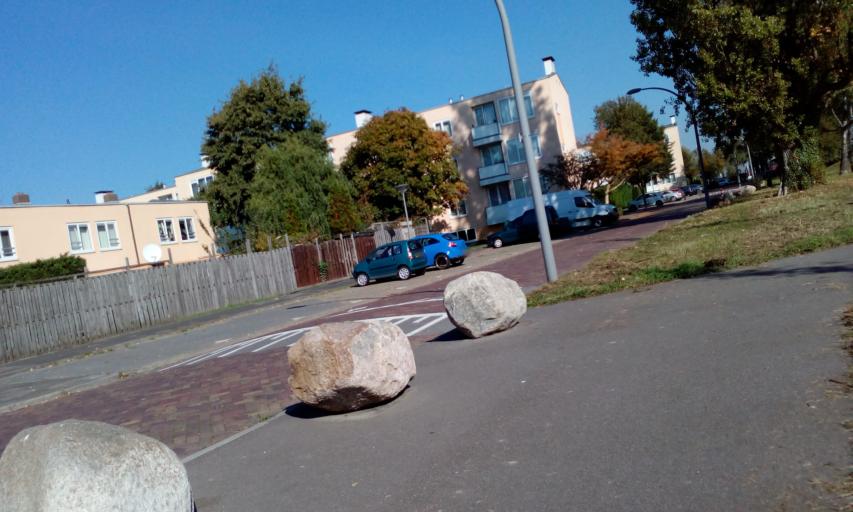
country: NL
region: South Holland
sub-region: Gemeente Vlaardingen
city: Vlaardingen
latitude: 51.9196
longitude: 4.3608
